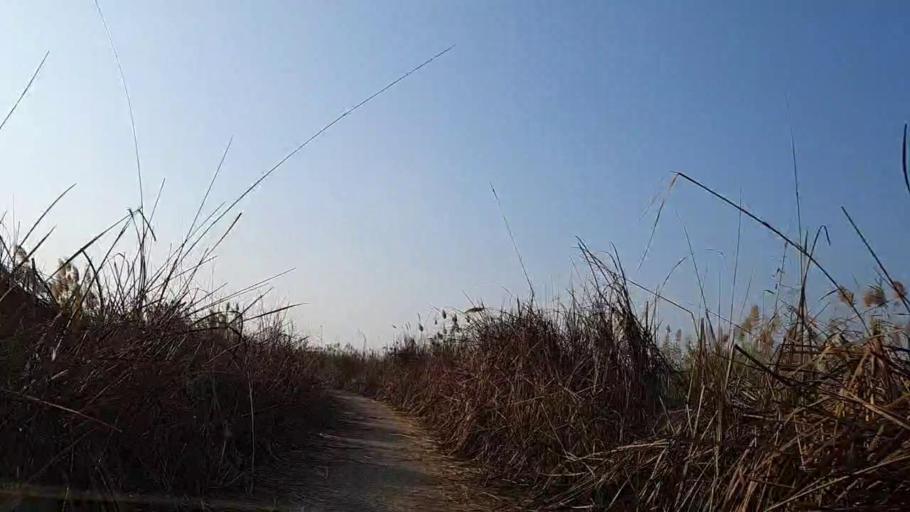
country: PK
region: Sindh
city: Sakrand
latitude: 26.0909
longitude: 68.3822
